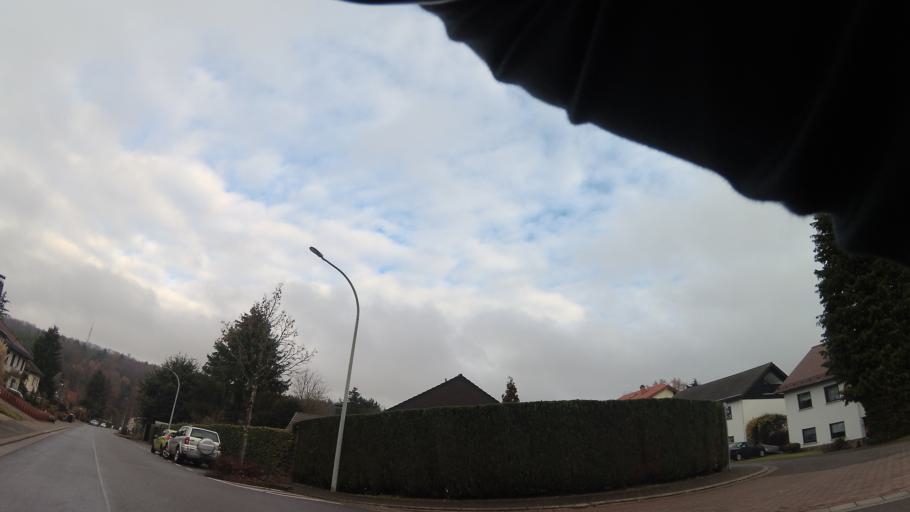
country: DE
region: Saarland
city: Spiesen-Elversberg
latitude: 49.3177
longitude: 7.1635
